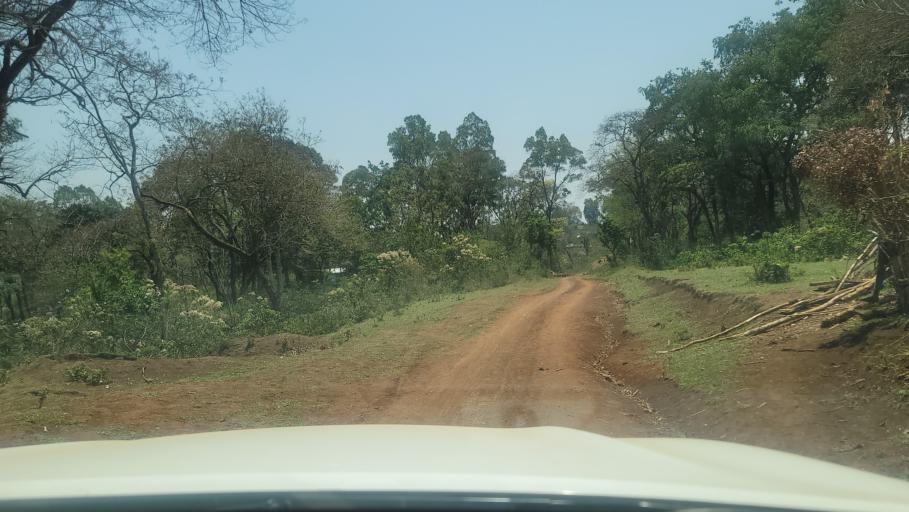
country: ET
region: Southern Nations, Nationalities, and People's Region
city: Bonga
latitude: 7.5345
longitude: 36.1864
